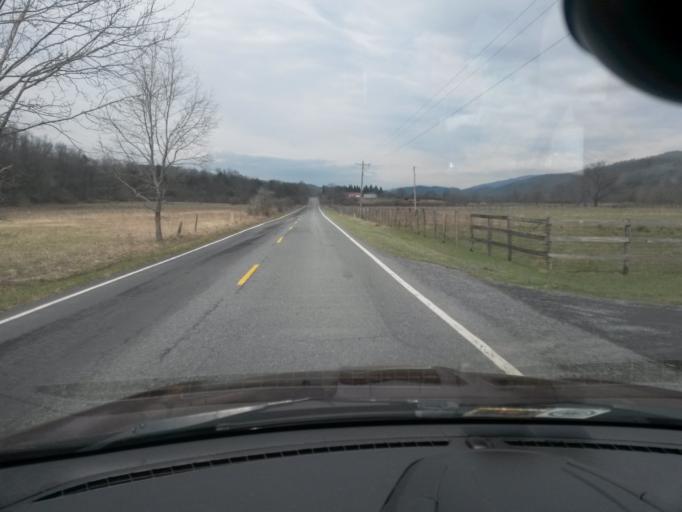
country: US
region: Virginia
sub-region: Highland County
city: Monterey
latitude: 38.2581
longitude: -79.6760
